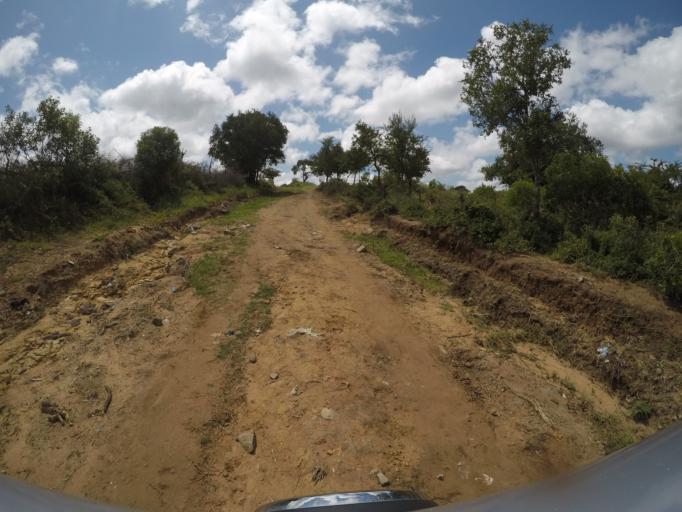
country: ZA
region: KwaZulu-Natal
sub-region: uThungulu District Municipality
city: Empangeni
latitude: -28.5843
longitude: 31.8425
